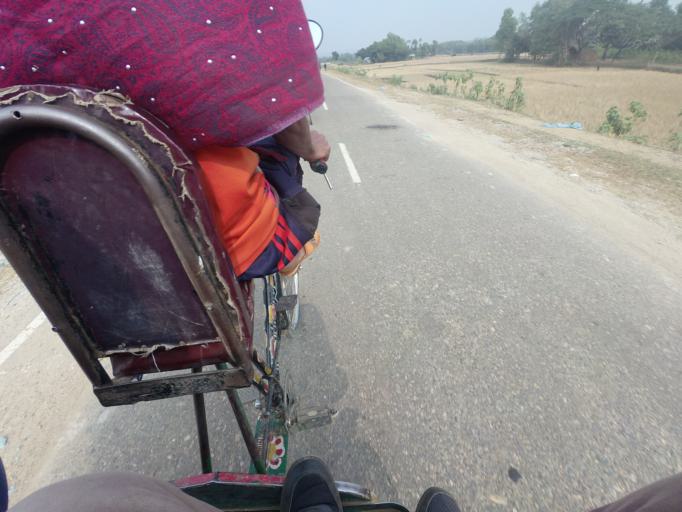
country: BD
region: Dhaka
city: Netrakona
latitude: 25.1532
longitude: 90.6591
